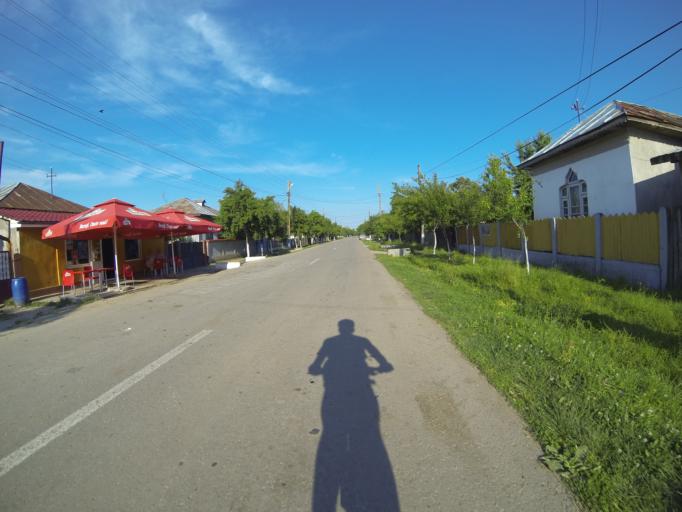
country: RO
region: Dolj
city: Satu Nou Calopar
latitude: 44.1593
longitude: 23.7835
